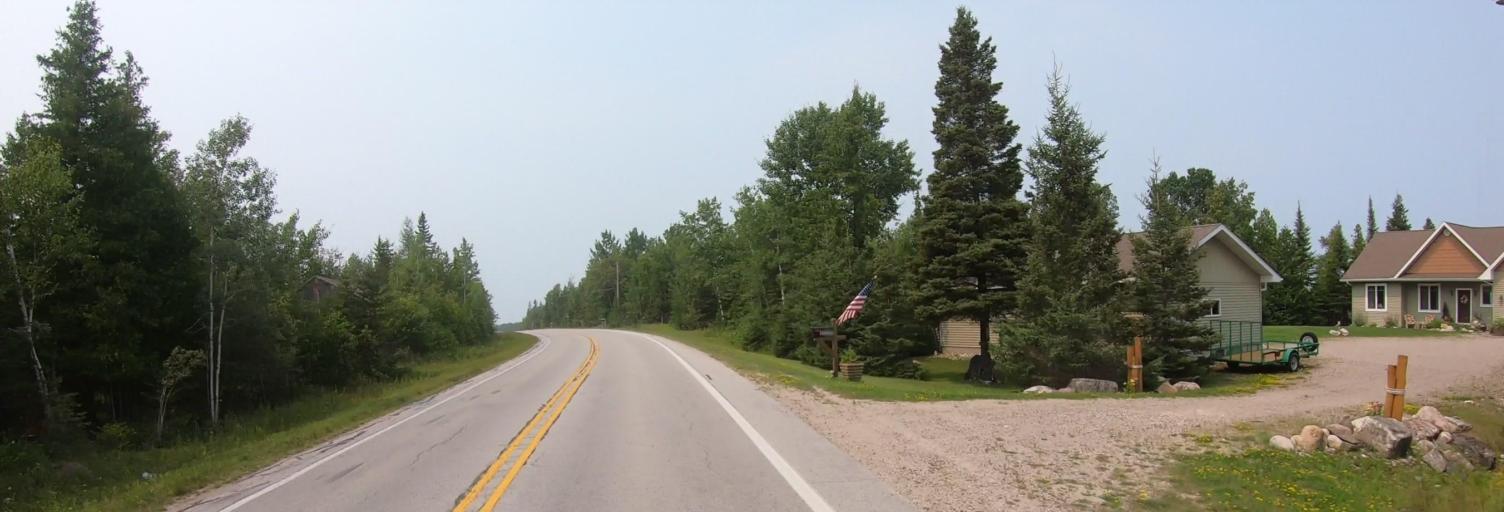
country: CA
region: Ontario
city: Thessalon
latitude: 45.9836
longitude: -83.8087
